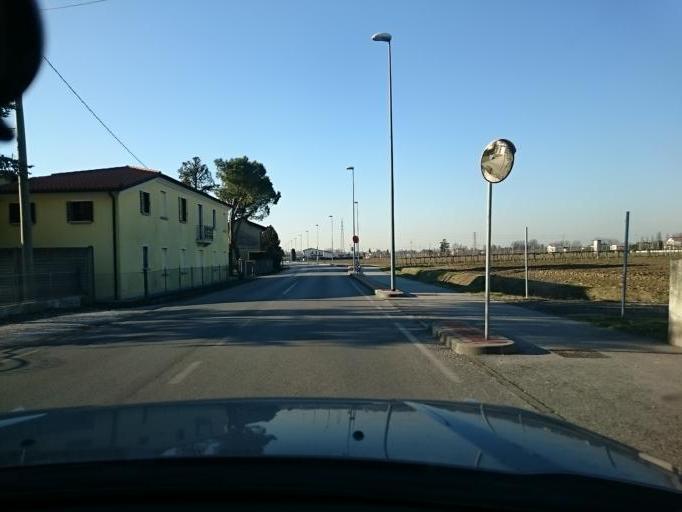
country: IT
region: Veneto
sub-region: Provincia di Venezia
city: Fiesso
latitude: 45.4061
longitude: 12.0392
